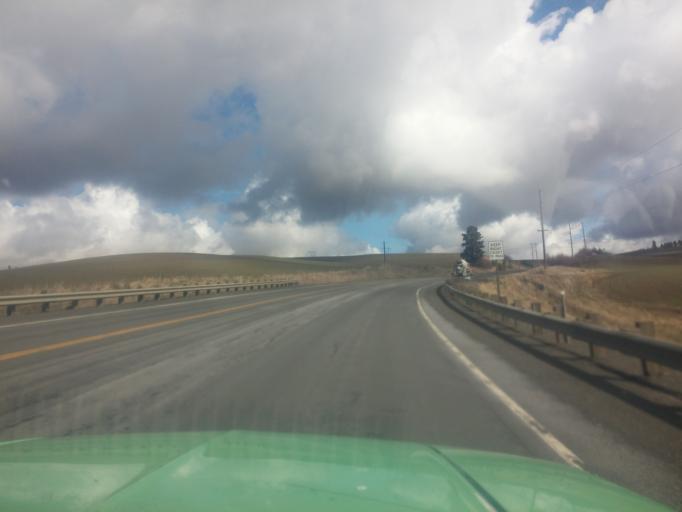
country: US
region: Idaho
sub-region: Latah County
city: Moscow
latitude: 46.8586
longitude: -117.0209
